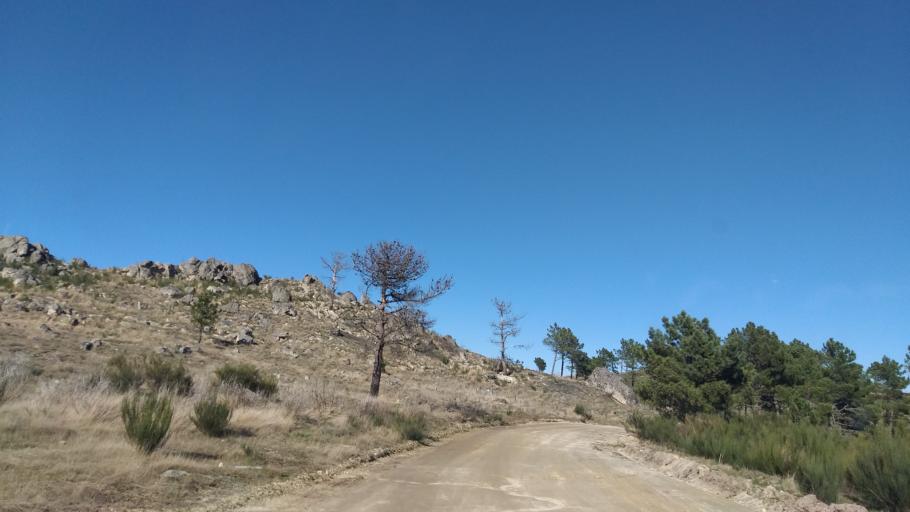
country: PT
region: Guarda
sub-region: Manteigas
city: Manteigas
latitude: 40.4999
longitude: -7.4895
